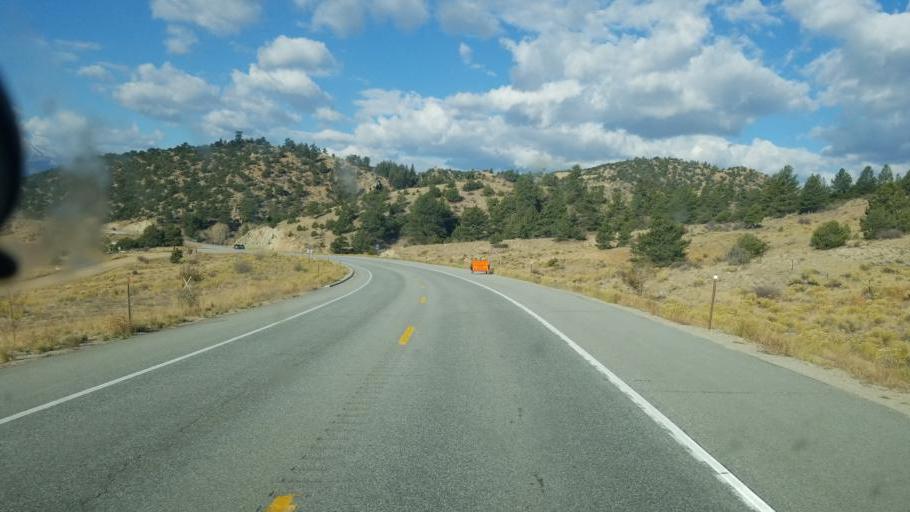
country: US
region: Colorado
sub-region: Chaffee County
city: Buena Vista
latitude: 38.8417
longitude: -106.0080
